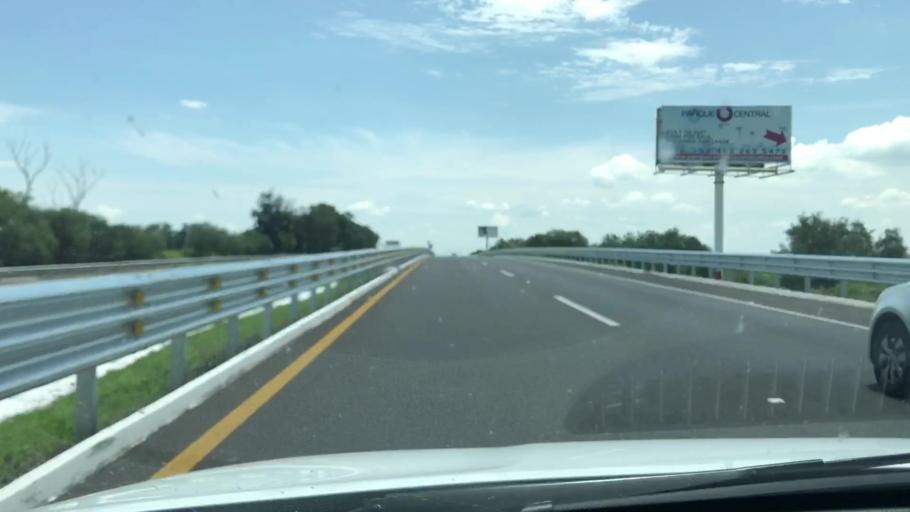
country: MX
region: Guanajuato
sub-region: Irapuato
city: Cuarta Brigada
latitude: 20.6505
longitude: -101.2828
